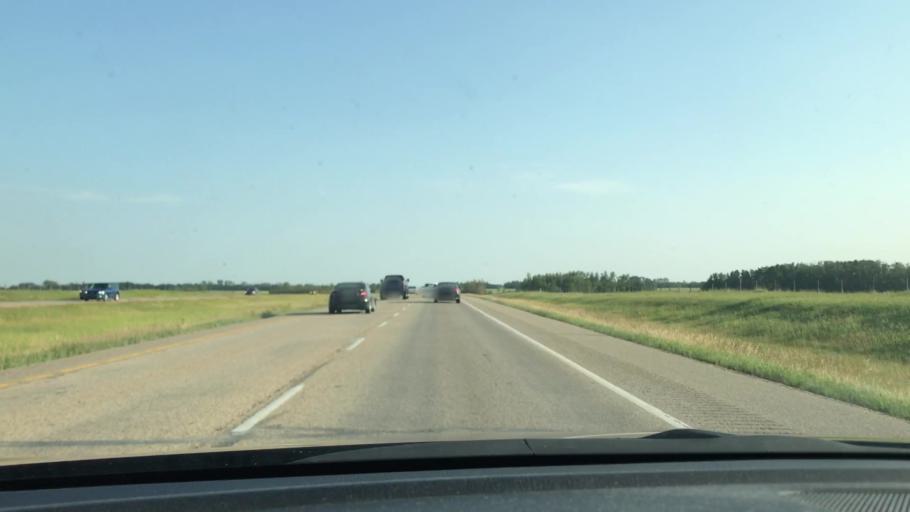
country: CA
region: Alberta
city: Millet
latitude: 53.1250
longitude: -113.5984
